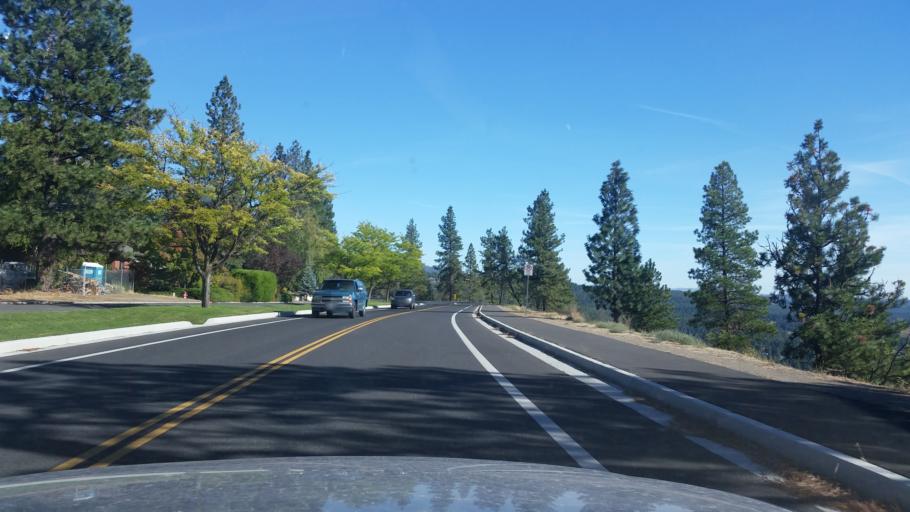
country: US
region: Washington
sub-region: Spokane County
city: Spokane
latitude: 47.6198
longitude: -117.4240
